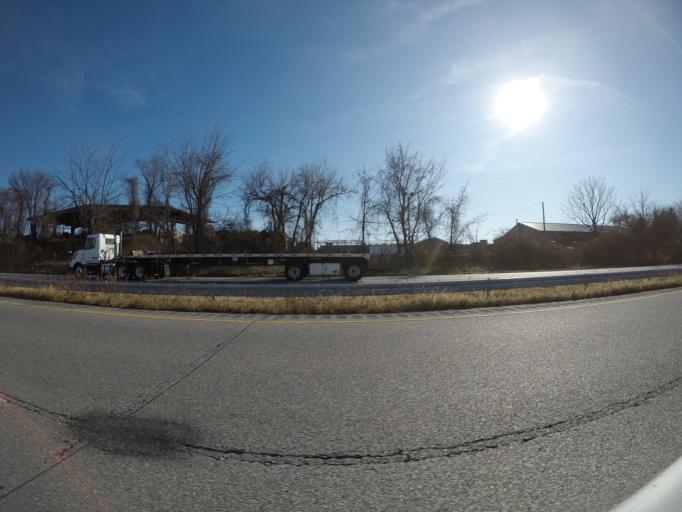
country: US
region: Pennsylvania
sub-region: Chester County
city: Parkesburg
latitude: 39.9869
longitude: -75.8844
